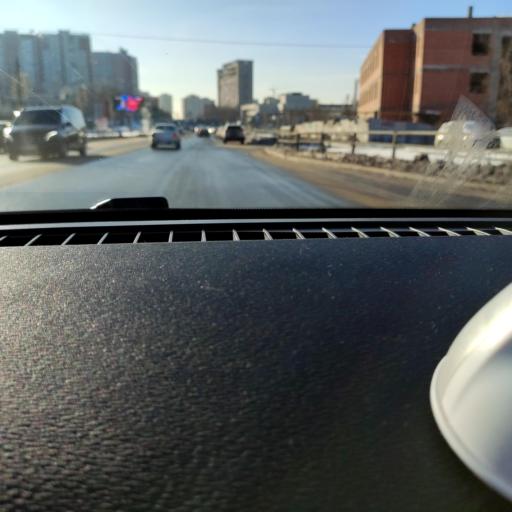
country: RU
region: Samara
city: Samara
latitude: 53.2638
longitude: 50.2102
